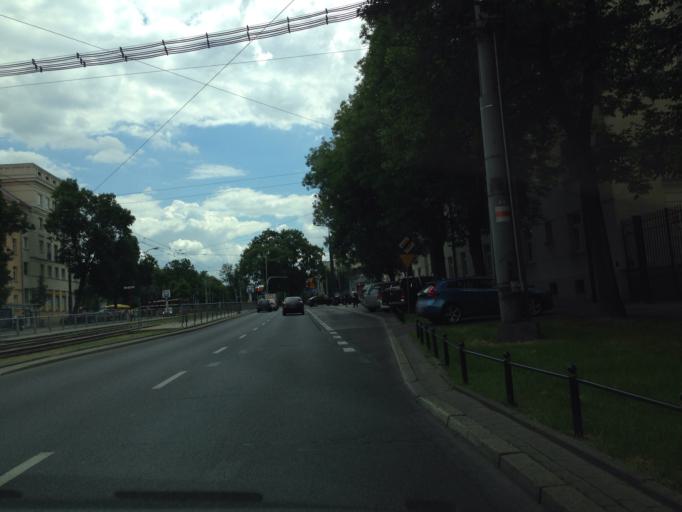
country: PL
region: Masovian Voivodeship
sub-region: Warszawa
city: Zoliborz
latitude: 52.2702
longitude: 20.9851
